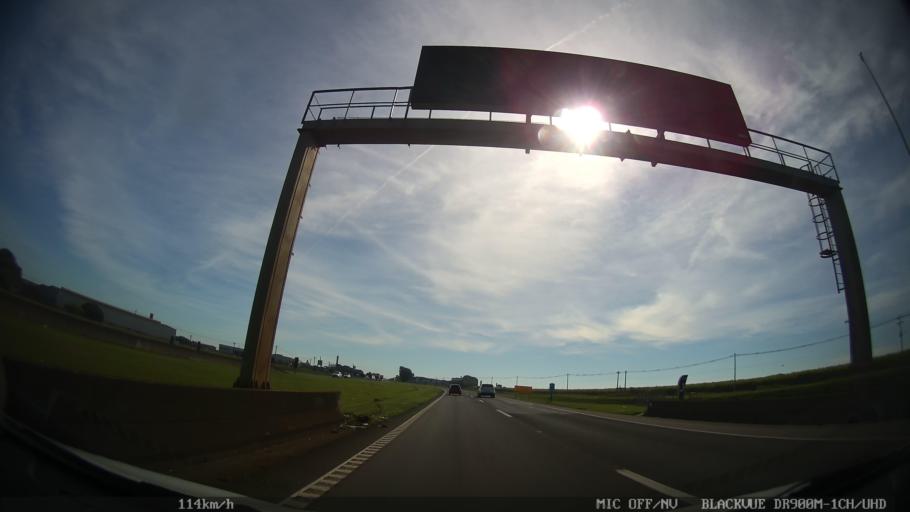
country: BR
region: Sao Paulo
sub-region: Araras
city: Araras
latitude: -22.4166
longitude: -47.3904
